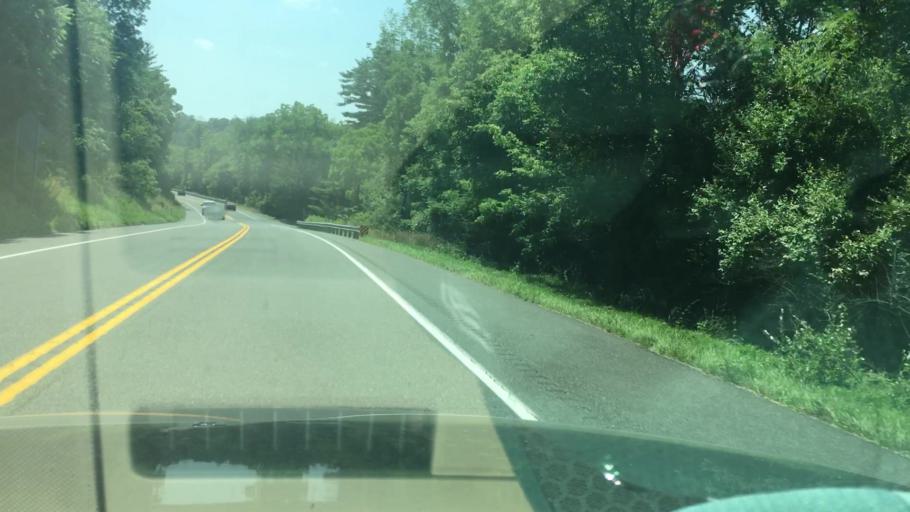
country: US
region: Pennsylvania
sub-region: Lehigh County
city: Schnecksville
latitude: 40.6663
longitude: -75.6871
